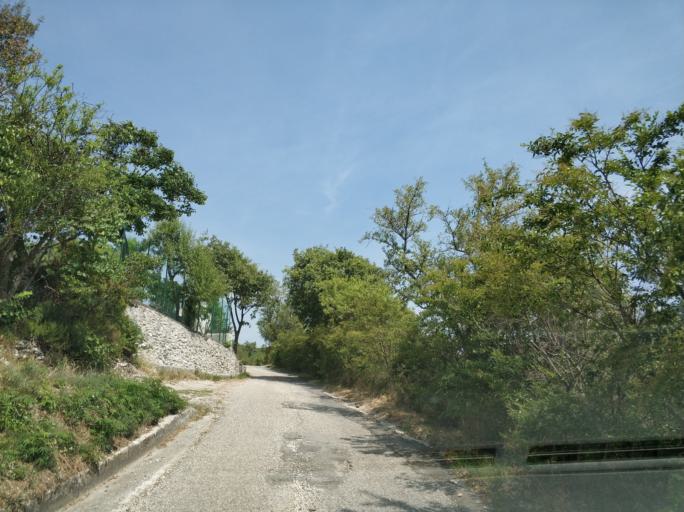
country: IT
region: Veneto
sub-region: Provincia di Padova
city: Arqua Petrarca
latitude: 45.2714
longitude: 11.7086
